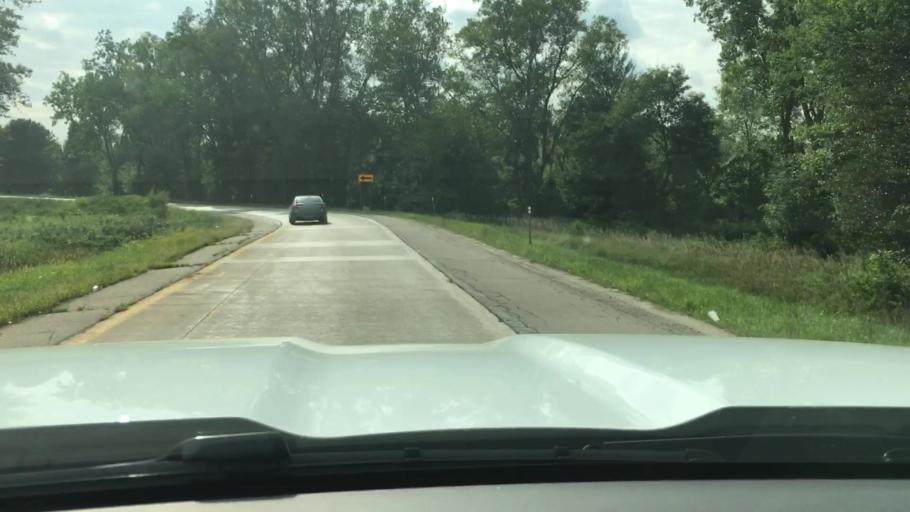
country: US
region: Michigan
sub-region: Eaton County
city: Dimondale
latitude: 42.6666
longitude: -84.5891
